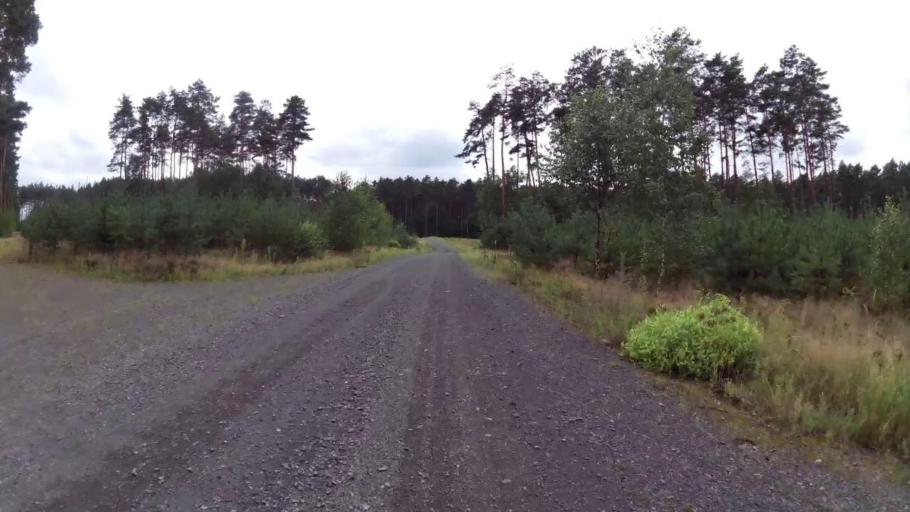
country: PL
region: West Pomeranian Voivodeship
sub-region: Powiat mysliborski
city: Debno
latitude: 52.7728
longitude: 14.7172
